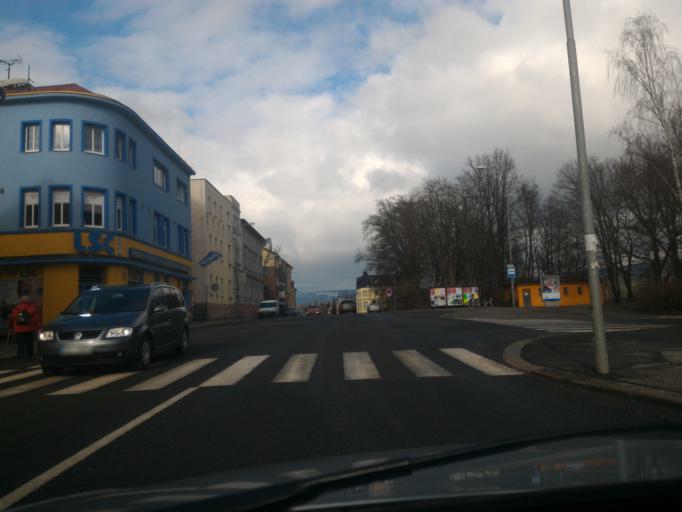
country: CZ
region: Liberecky
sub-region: Okres Jablonec nad Nisou
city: Jablonec nad Nisou
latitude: 50.7272
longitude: 15.1705
